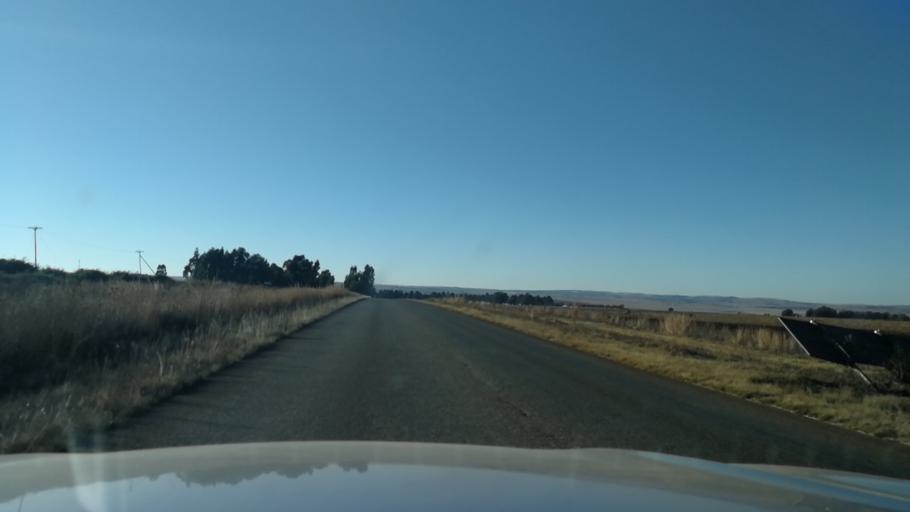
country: ZA
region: North-West
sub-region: Bojanala Platinum District Municipality
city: Rustenburg
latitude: -25.9665
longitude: 27.2192
